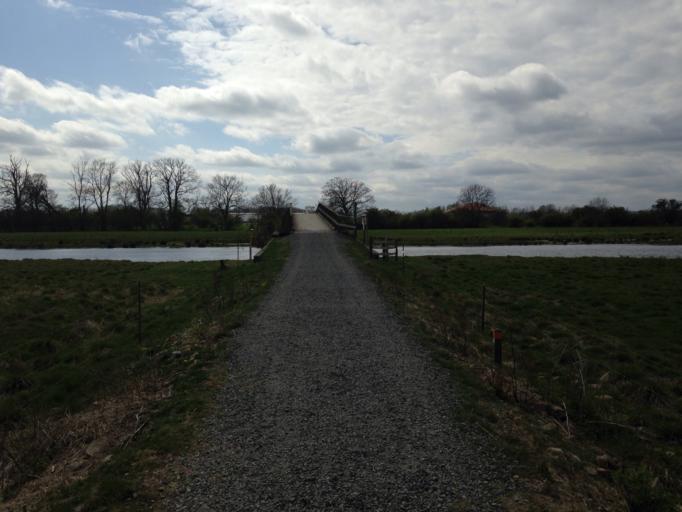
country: SE
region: Skane
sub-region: Kristianstads Kommun
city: Kristianstad
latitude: 56.0393
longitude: 14.1259
